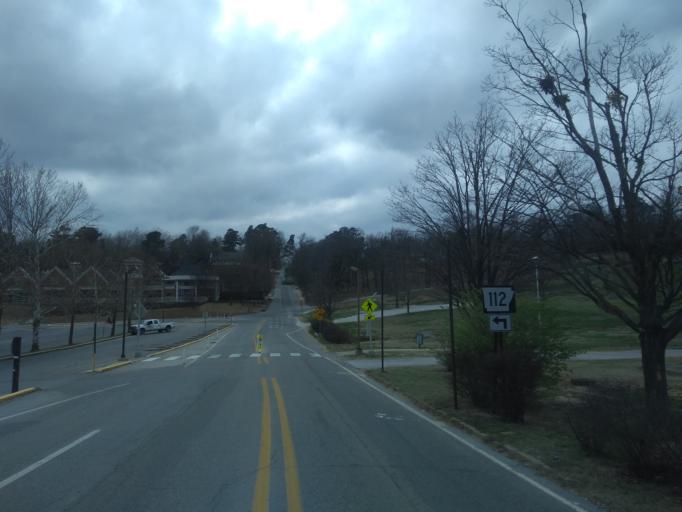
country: US
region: Arkansas
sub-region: Washington County
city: Fayetteville
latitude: 36.0704
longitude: -94.1786
